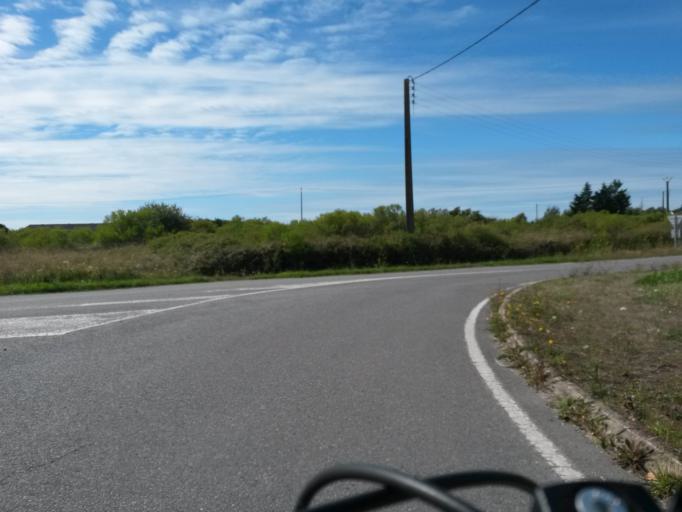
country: FR
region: Pays de la Loire
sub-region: Departement de la Loire-Atlantique
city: Guerande
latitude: 47.3028
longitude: -2.4313
